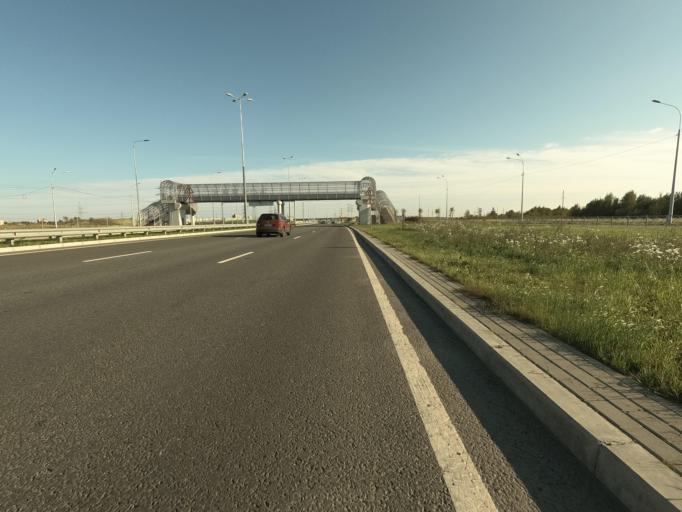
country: RU
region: St.-Petersburg
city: Kolpino
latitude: 59.7464
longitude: 30.5345
